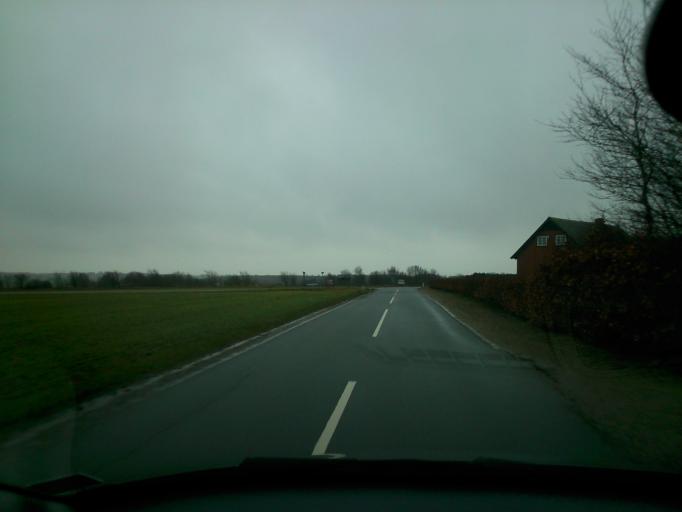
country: DK
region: Central Jutland
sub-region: Ringkobing-Skjern Kommune
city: Skjern
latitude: 56.0513
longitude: 8.4528
